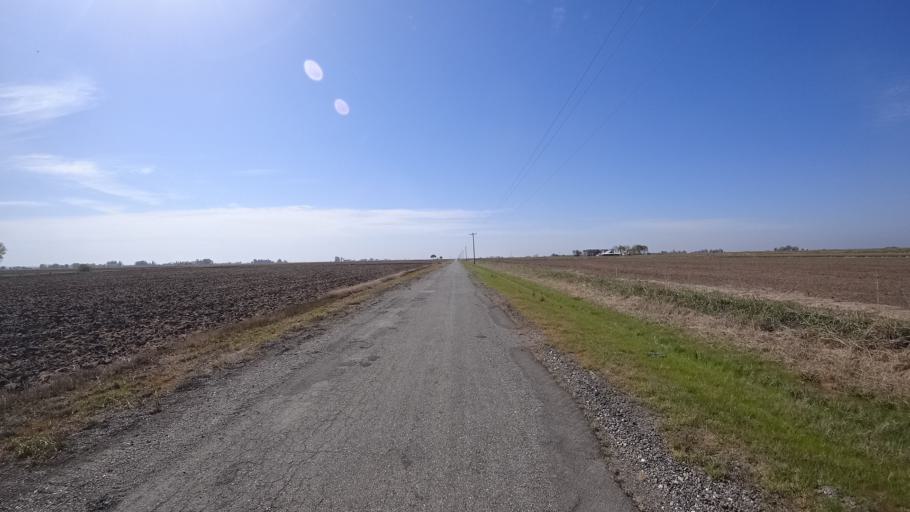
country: US
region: California
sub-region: Glenn County
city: Hamilton City
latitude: 39.6146
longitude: -122.0744
